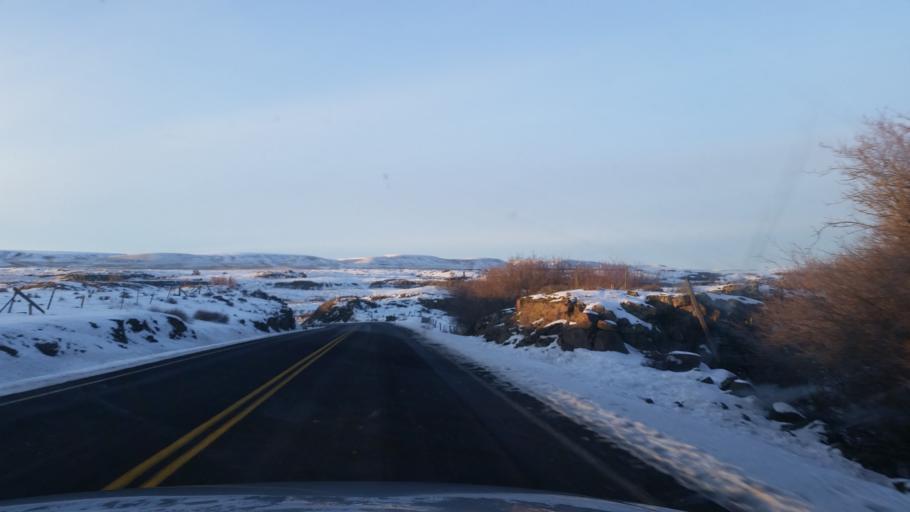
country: US
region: Washington
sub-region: Spokane County
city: Cheney
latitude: 47.1200
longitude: -117.7456
